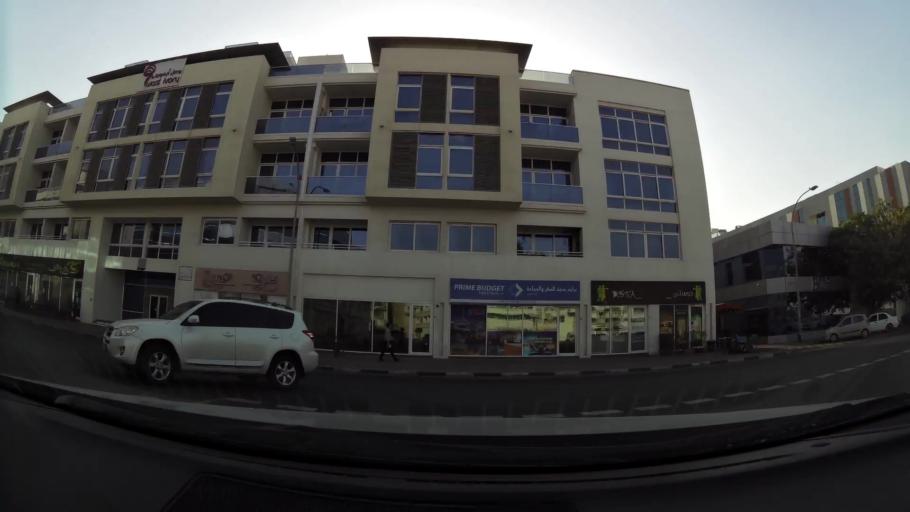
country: AE
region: Ash Shariqah
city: Sharjah
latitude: 25.2464
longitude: 55.3103
